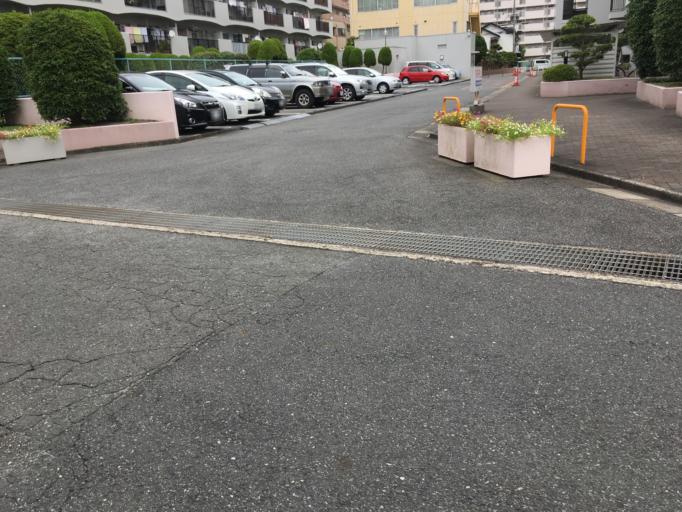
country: JP
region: Nara
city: Nara-shi
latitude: 34.6828
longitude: 135.8077
